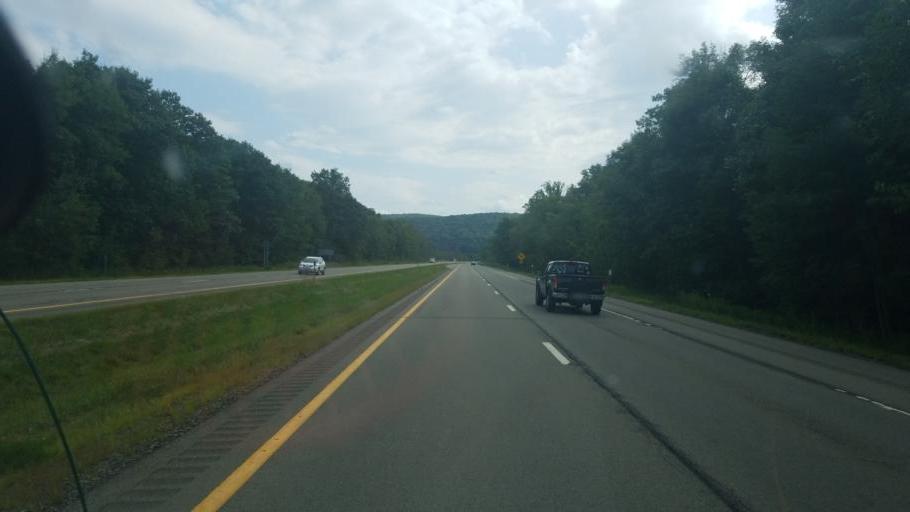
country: US
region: New York
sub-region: Cattaraugus County
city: Salamanca
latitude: 42.1200
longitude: -78.7783
